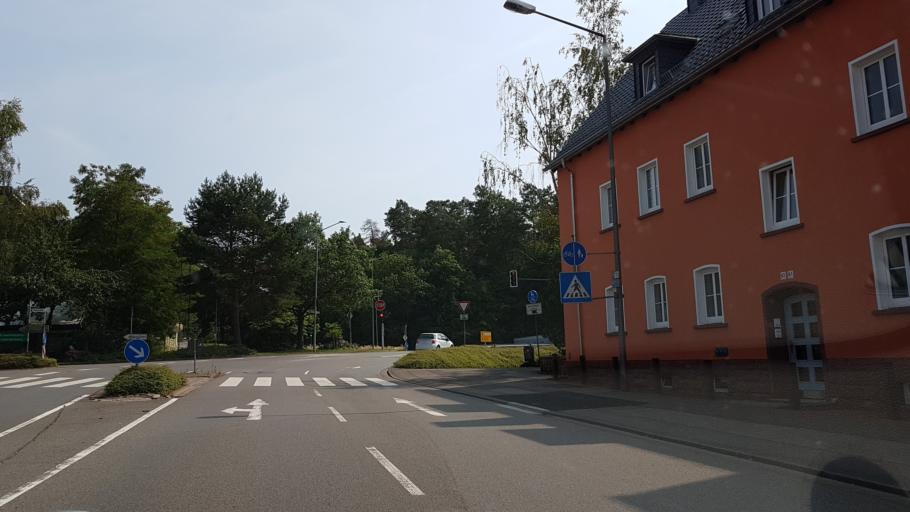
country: DE
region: Saarland
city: Homburg
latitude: 49.3130
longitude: 7.3438
